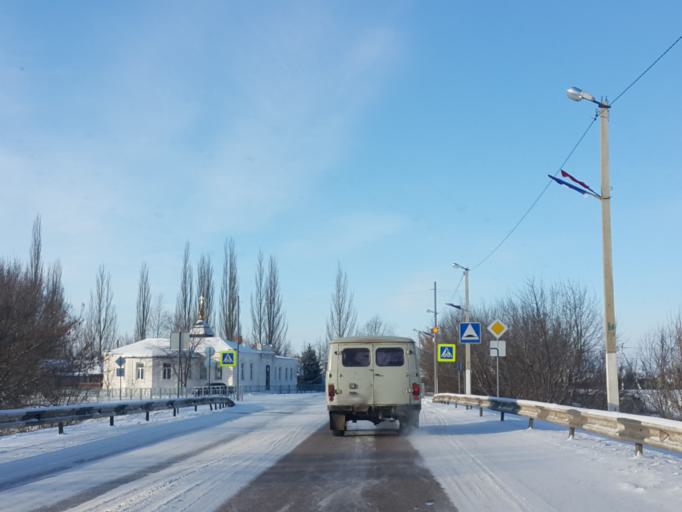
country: RU
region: Tambov
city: Znamenka
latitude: 52.4182
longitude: 41.4327
